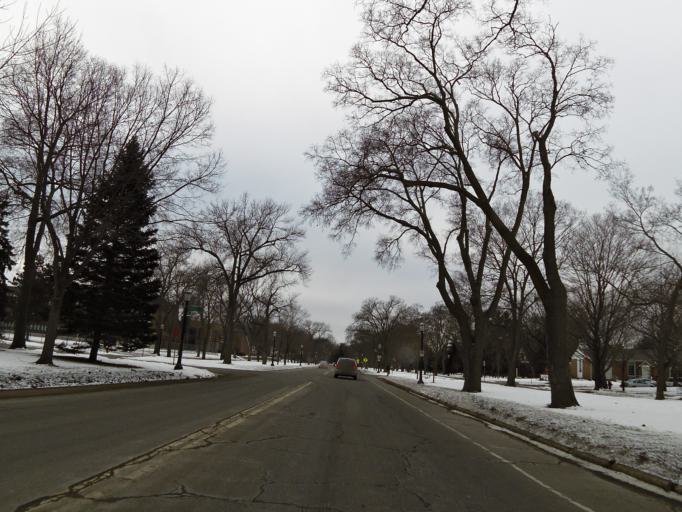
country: US
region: Minnesota
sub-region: Ramsey County
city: Falcon Heights
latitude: 44.9415
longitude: -93.1699
